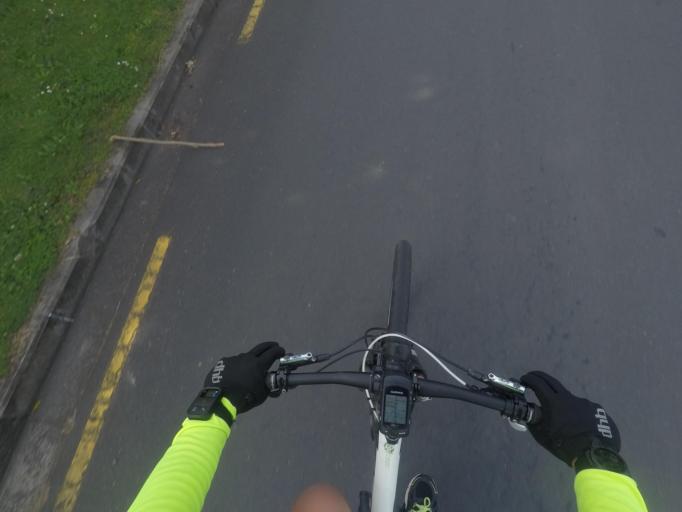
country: NZ
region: Auckland
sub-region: Auckland
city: Mangere
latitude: -36.9188
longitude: 174.7826
